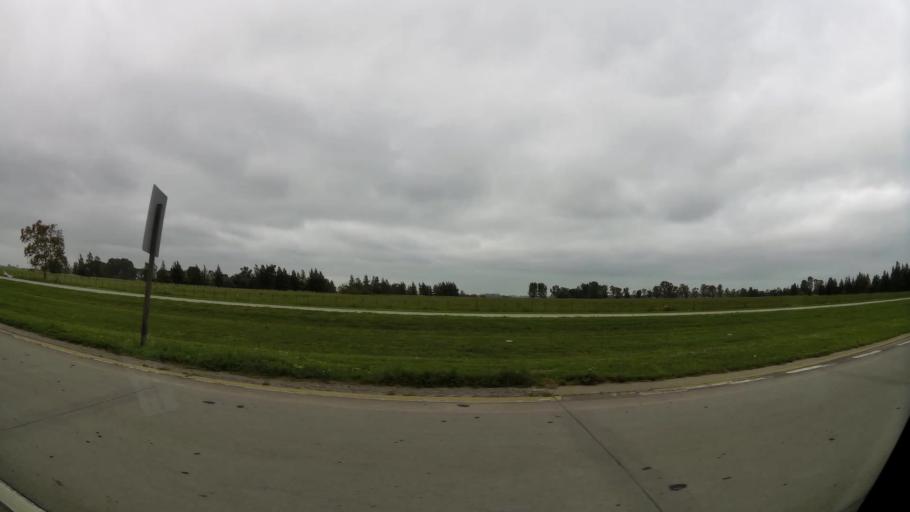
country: AR
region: Buenos Aires
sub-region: Partido de Brandsen
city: Brandsen
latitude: -35.0441
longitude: -58.1660
